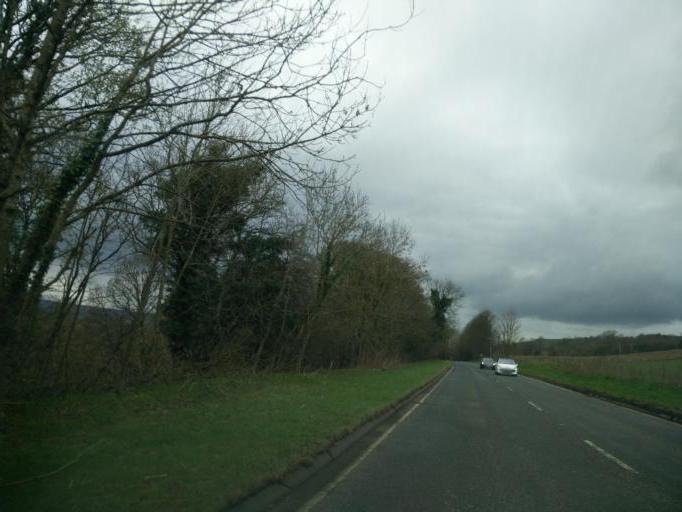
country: GB
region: England
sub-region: County Durham
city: Wolsingham
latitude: 54.7277
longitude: -1.9311
